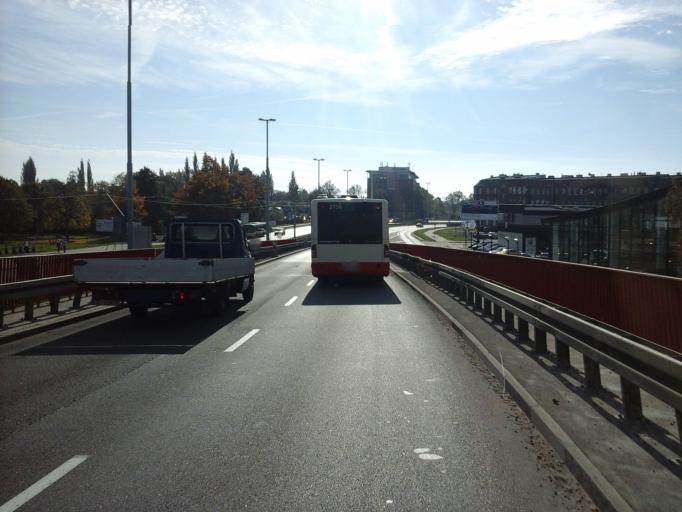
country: PL
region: Pomeranian Voivodeship
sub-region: Gdansk
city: Gdansk
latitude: 54.3479
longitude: 18.6691
